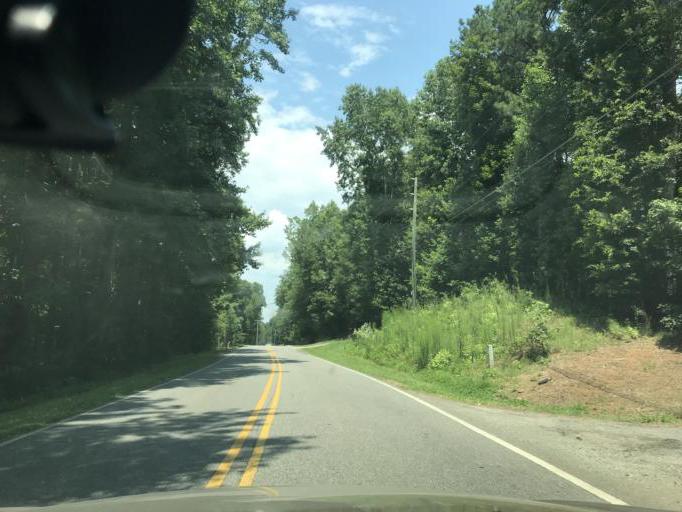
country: US
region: Georgia
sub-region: Forsyth County
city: Cumming
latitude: 34.3038
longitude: -84.1578
